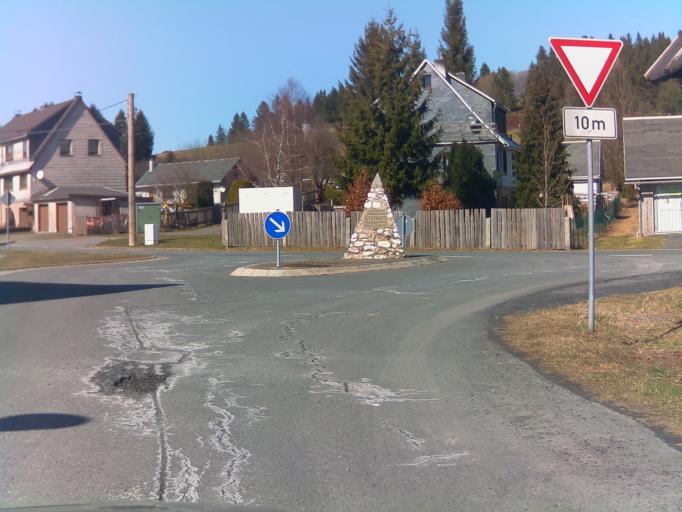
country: DE
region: Thuringia
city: Steinheid
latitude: 50.4615
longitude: 11.0908
